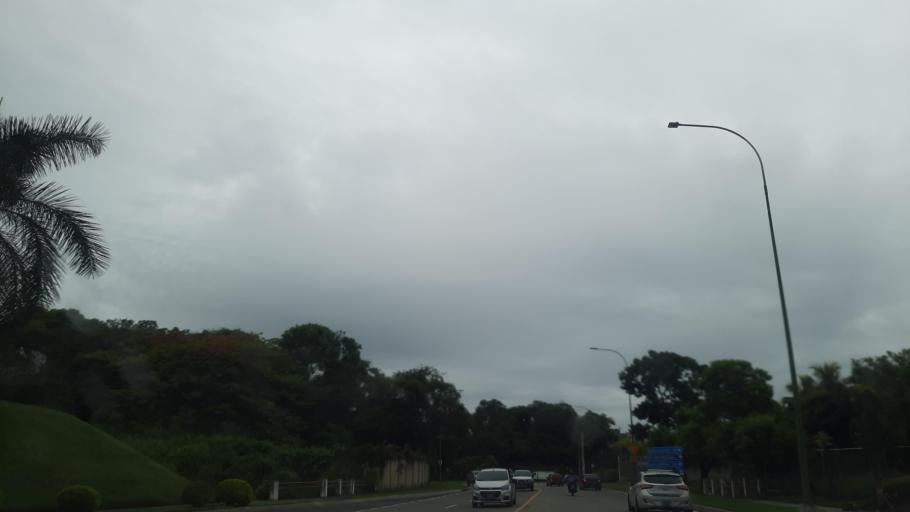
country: SV
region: La Libertad
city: Antiguo Cuscatlan
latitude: 13.6855
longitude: -89.2461
